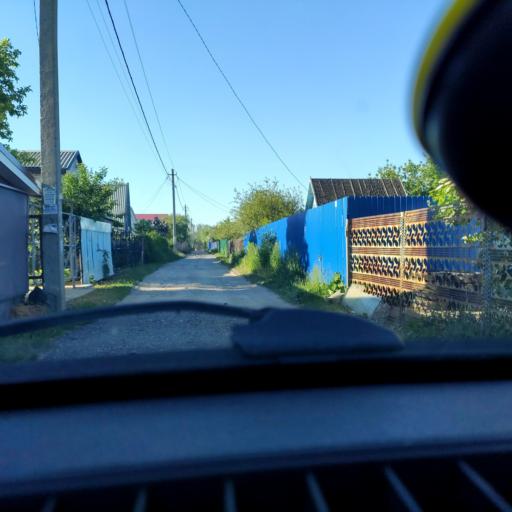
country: RU
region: Samara
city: Tol'yatti
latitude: 53.5944
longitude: 49.3147
